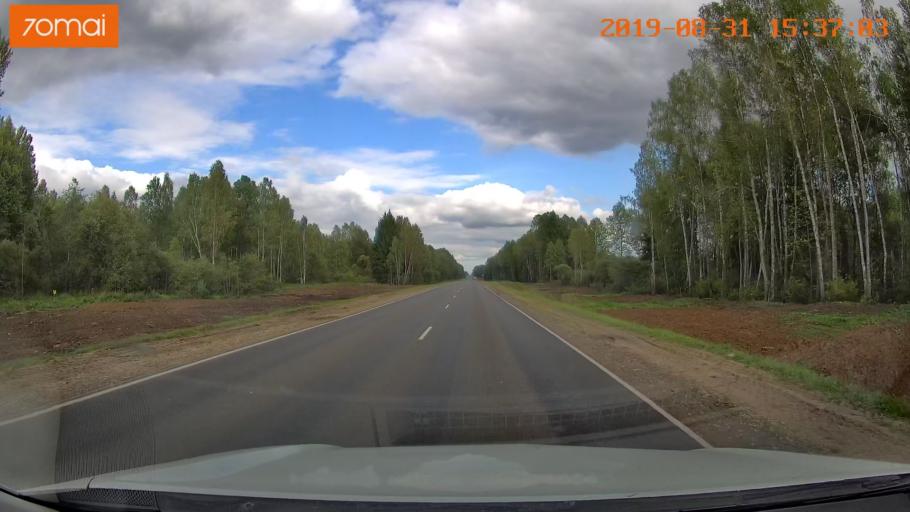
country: RU
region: Kaluga
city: Mosal'sk
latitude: 54.6155
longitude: 34.7745
